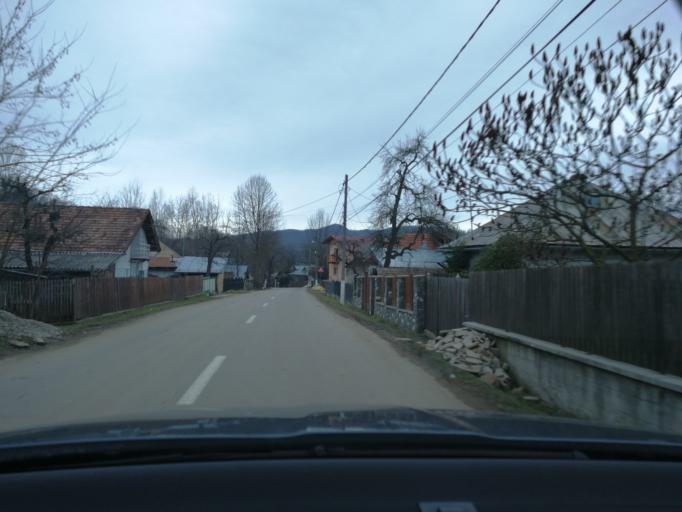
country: RO
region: Prahova
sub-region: Comuna Adunati
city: Ocina de Sus
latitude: 45.1859
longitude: 25.6076
